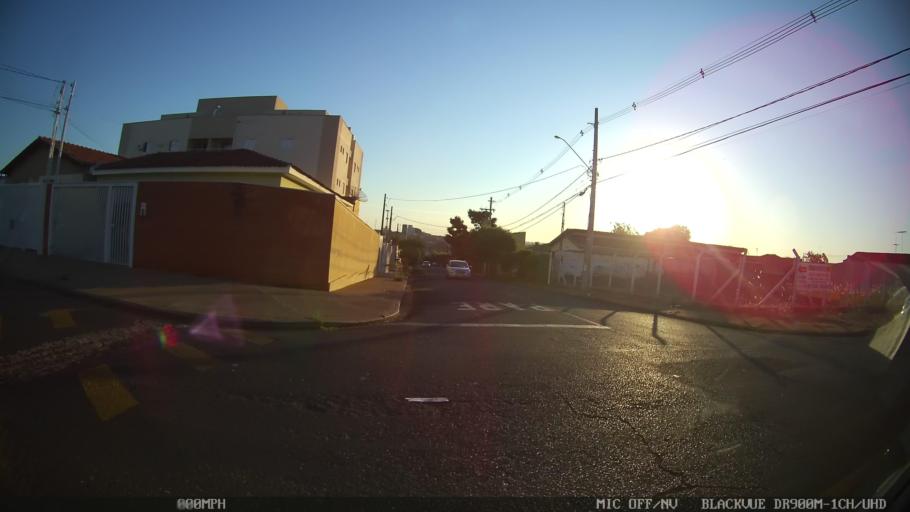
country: BR
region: Sao Paulo
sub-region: Sao Jose Do Rio Preto
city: Sao Jose do Rio Preto
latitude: -20.7934
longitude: -49.3707
